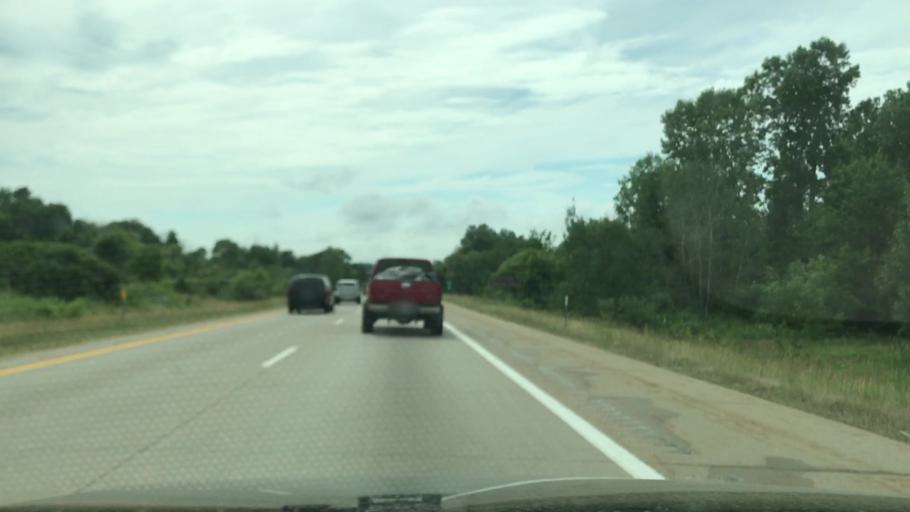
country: US
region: Michigan
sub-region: Kent County
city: Walker
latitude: 43.0181
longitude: -85.7503
